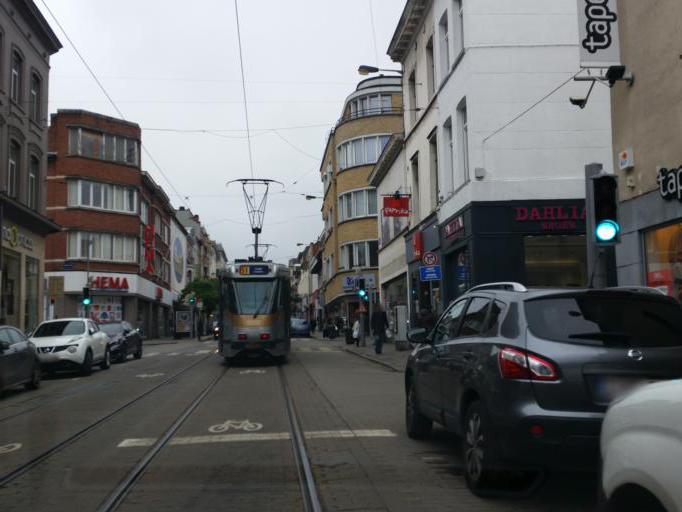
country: BE
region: Flanders
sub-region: Provincie Vlaams-Brabant
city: Drogenbos
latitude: 50.8030
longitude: 4.3366
